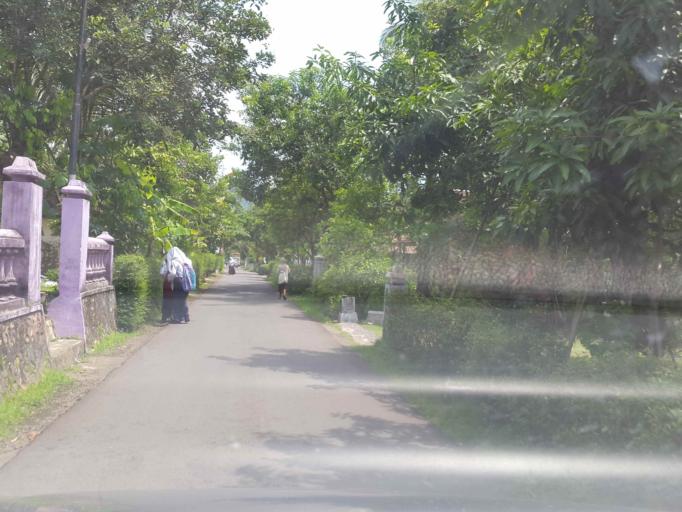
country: ID
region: Central Java
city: Kutoarjo
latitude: -7.6413
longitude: 110.0559
